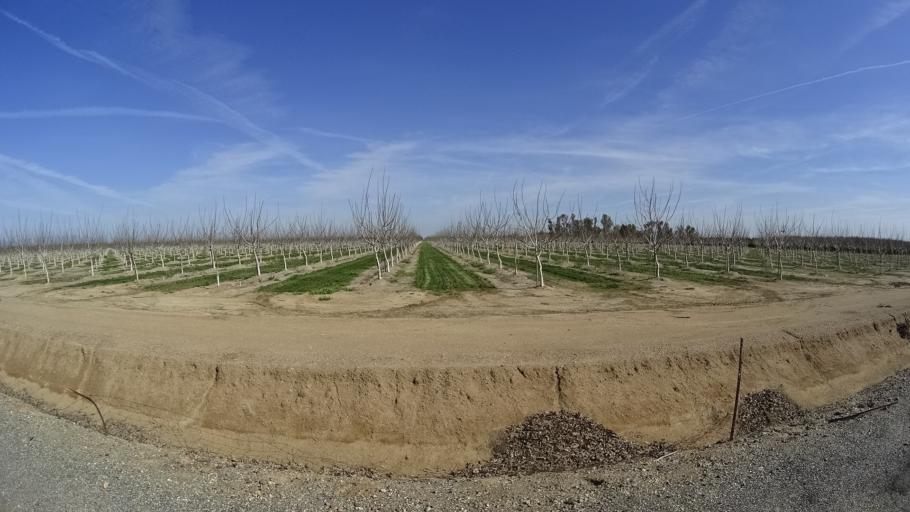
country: US
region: California
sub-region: Glenn County
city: Willows
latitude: 39.6115
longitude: -122.2144
